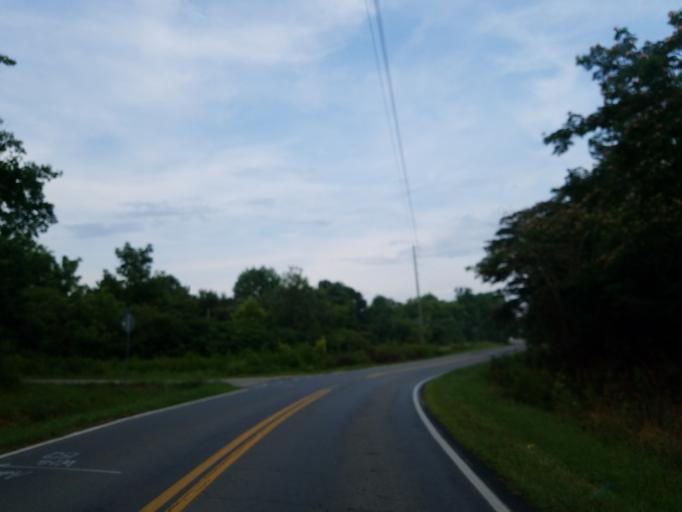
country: US
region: Georgia
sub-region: Pickens County
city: Jasper
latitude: 34.4575
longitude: -84.5421
